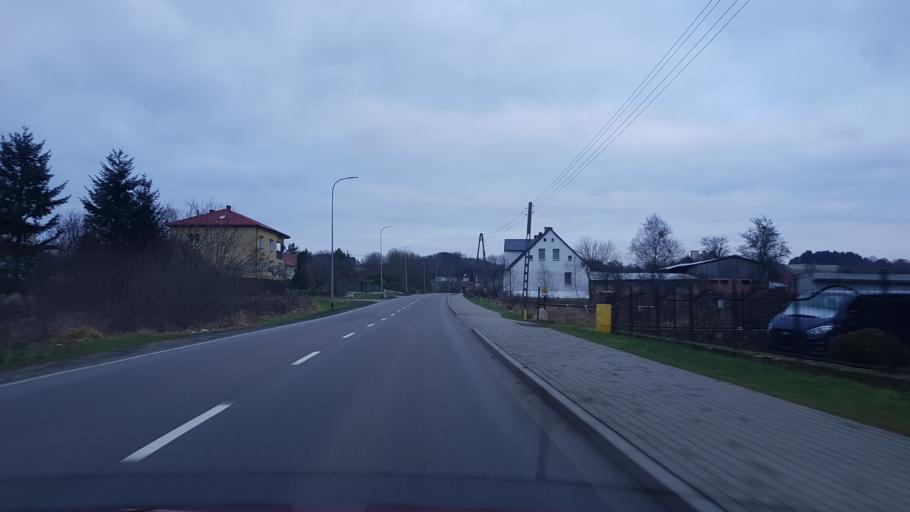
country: PL
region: Pomeranian Voivodeship
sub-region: Powiat bytowski
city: Miastko
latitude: 54.0043
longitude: 16.9901
